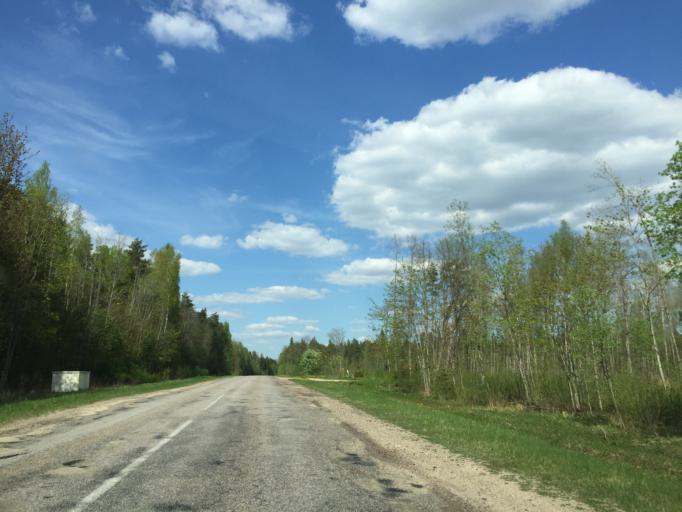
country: LV
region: Limbazu Rajons
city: Limbazi
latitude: 57.4114
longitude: 24.6950
